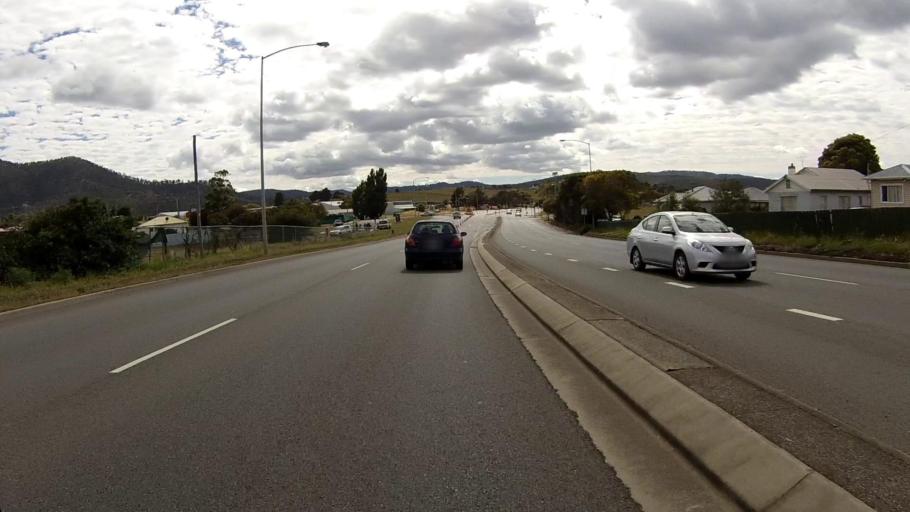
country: AU
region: Tasmania
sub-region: Glenorchy
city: Goodwood
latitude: -42.8238
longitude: 147.2927
